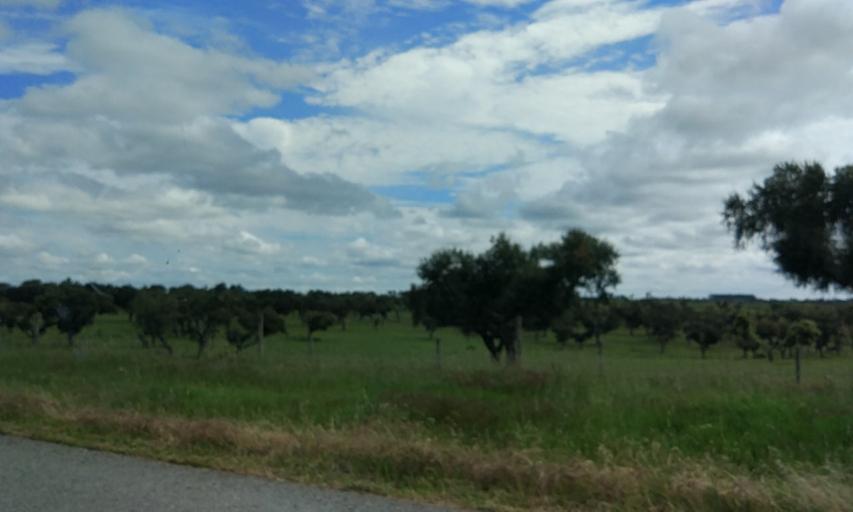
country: PT
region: Evora
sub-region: Vendas Novas
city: Vendas Novas
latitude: 38.6460
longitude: -8.3936
